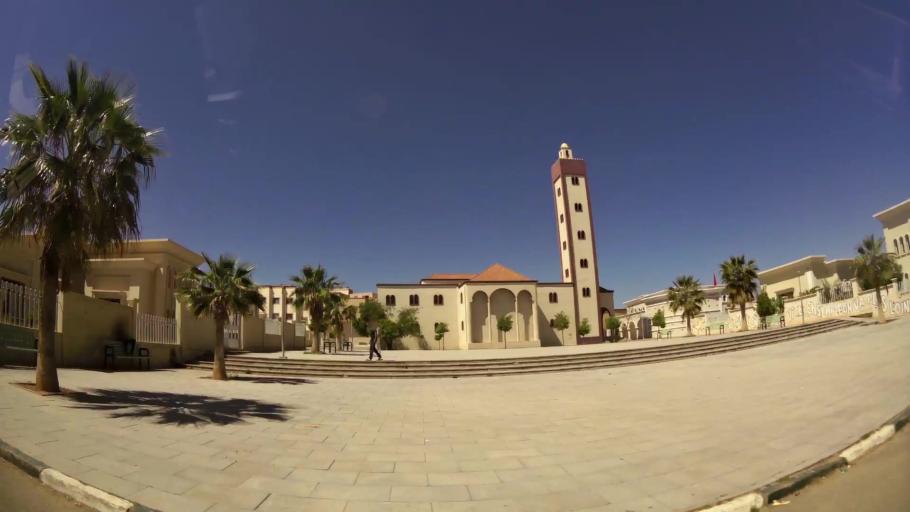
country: MA
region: Oriental
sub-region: Oujda-Angad
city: Oujda
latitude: 34.6551
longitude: -1.8743
